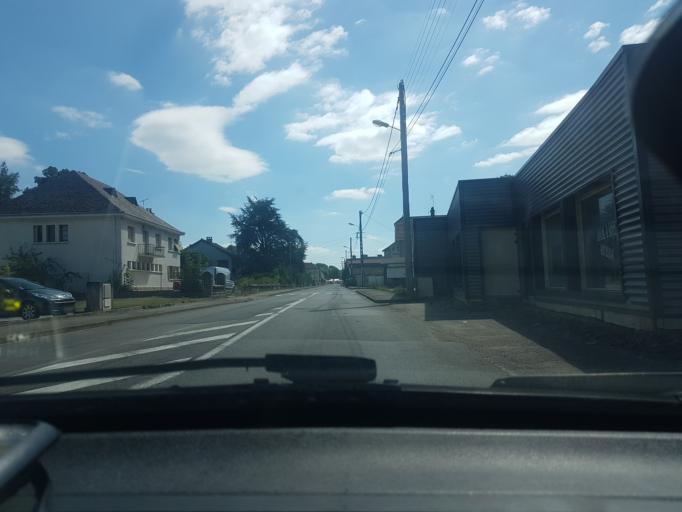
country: FR
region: Franche-Comte
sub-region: Departement de la Haute-Saone
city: Gray
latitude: 47.4441
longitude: 5.5984
